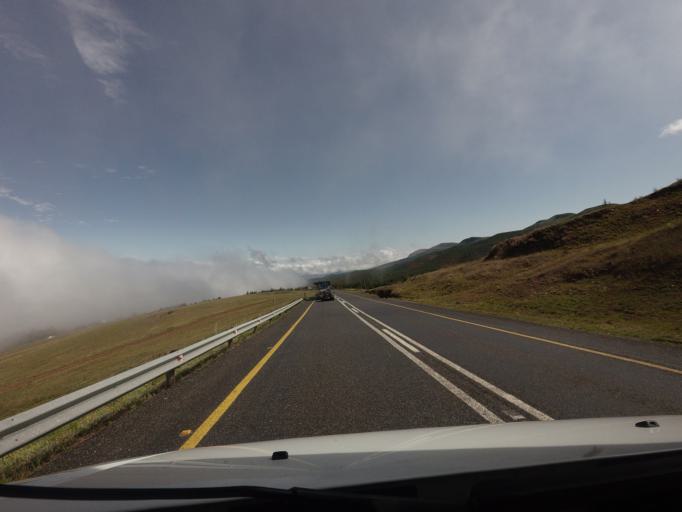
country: ZA
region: Mpumalanga
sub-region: Ehlanzeni District
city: Lydenburg
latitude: -25.1621
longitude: 30.6281
